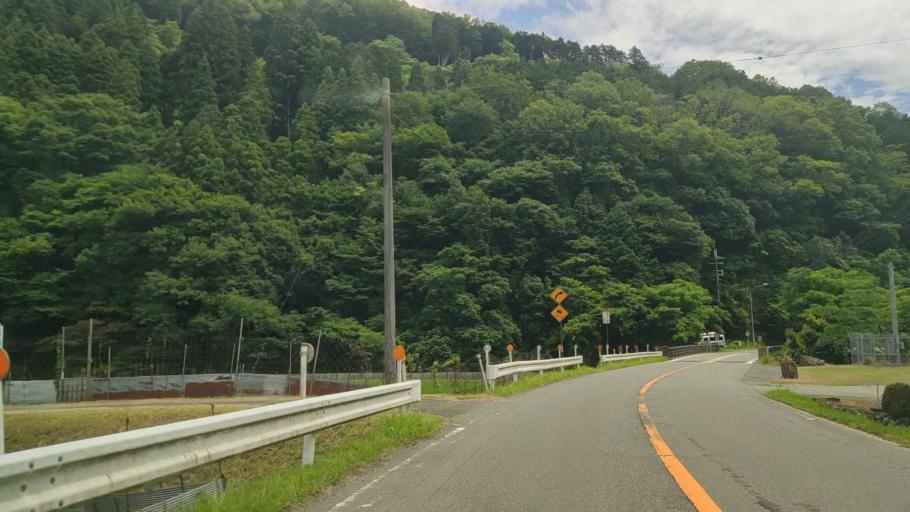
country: JP
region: Hyogo
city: Yamazakicho-nakabirose
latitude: 35.0794
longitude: 134.3603
